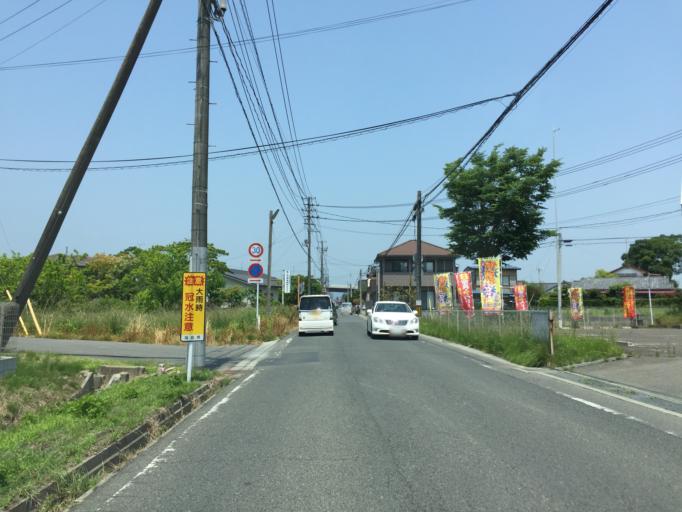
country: JP
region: Miyagi
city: Marumori
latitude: 37.7892
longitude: 140.9278
